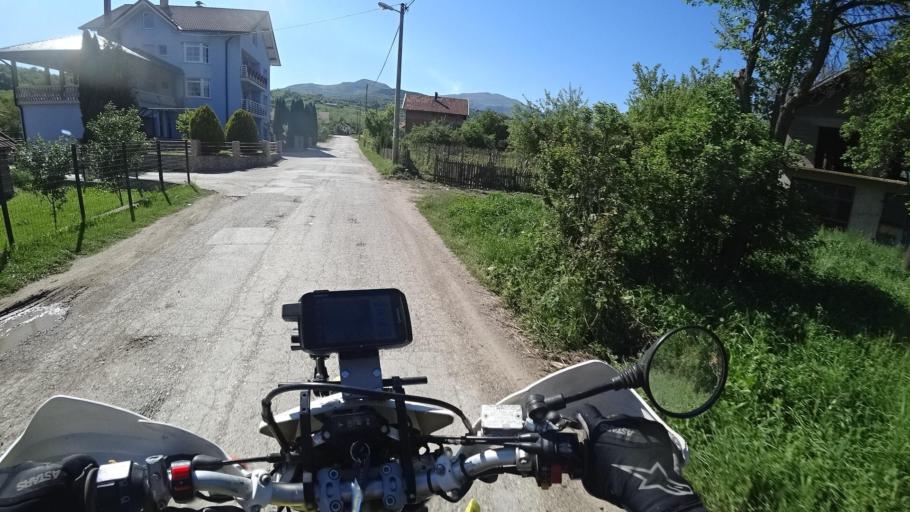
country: BA
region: Federation of Bosnia and Herzegovina
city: Travnik
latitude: 44.2393
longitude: 17.7563
